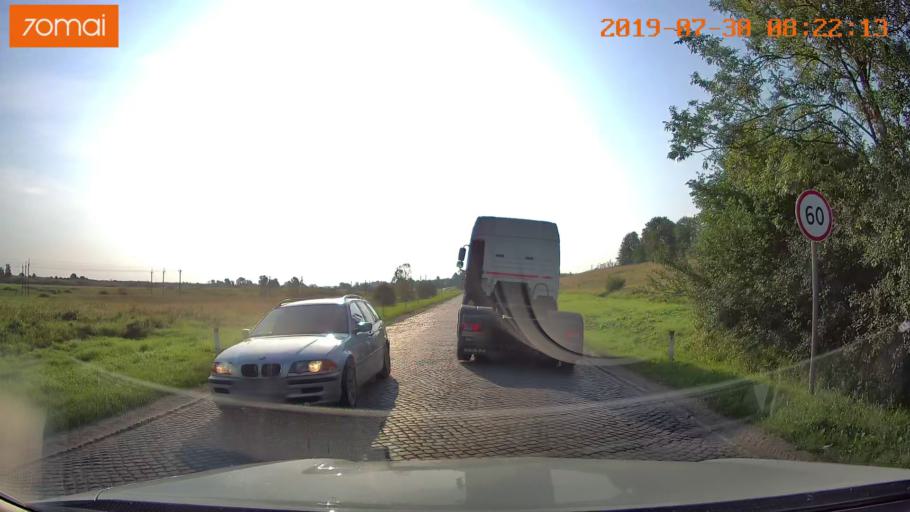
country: RU
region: Kaliningrad
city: Chernyakhovsk
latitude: 54.6257
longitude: 21.5321
